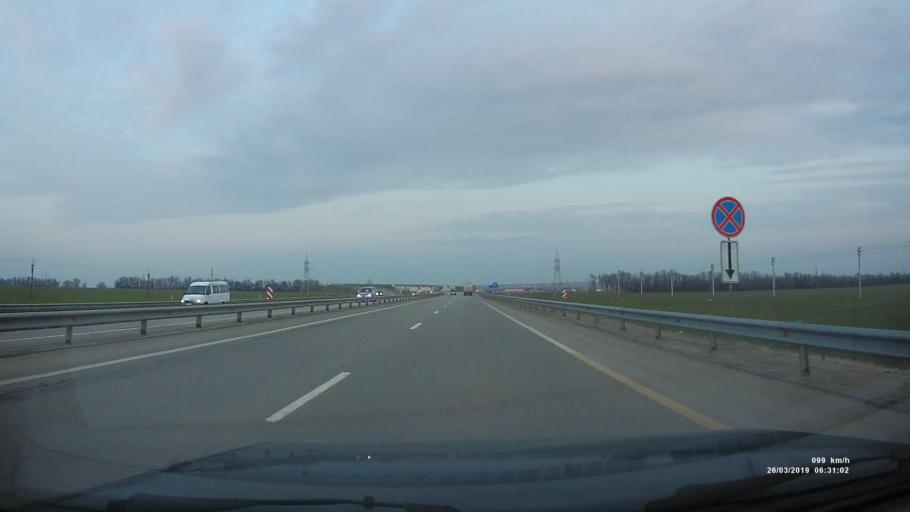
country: RU
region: Rostov
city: Krym
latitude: 47.2726
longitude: 39.5403
